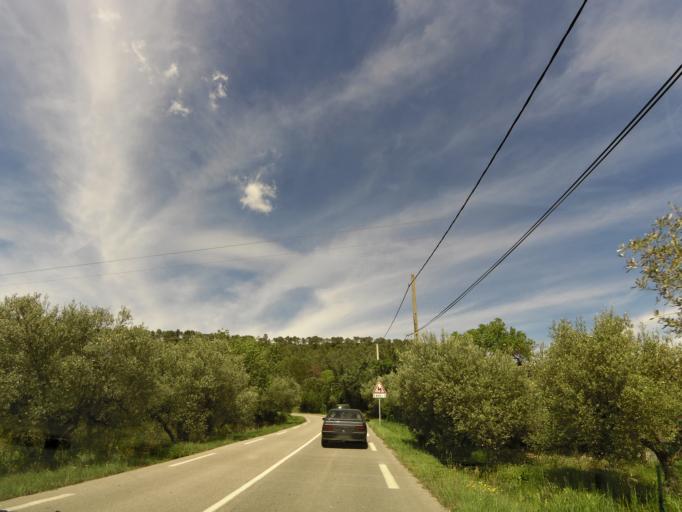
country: FR
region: Languedoc-Roussillon
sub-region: Departement du Gard
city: Quissac
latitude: 43.8416
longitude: 4.0289
